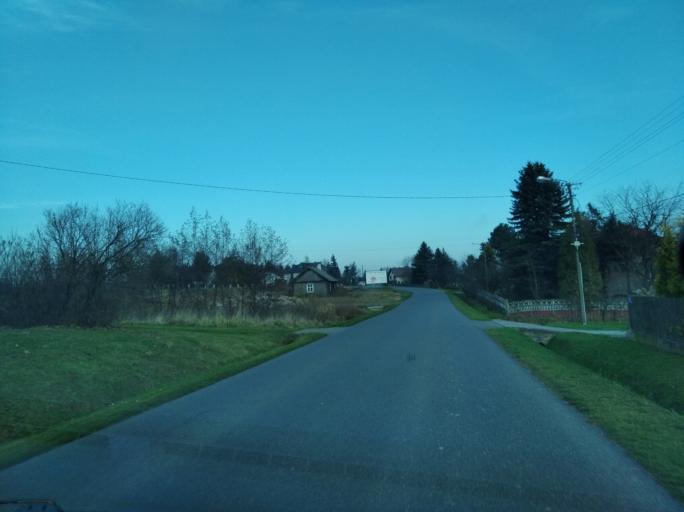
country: PL
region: Subcarpathian Voivodeship
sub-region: Powiat ropczycko-sedziszowski
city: Iwierzyce
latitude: 50.0014
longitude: 21.7518
